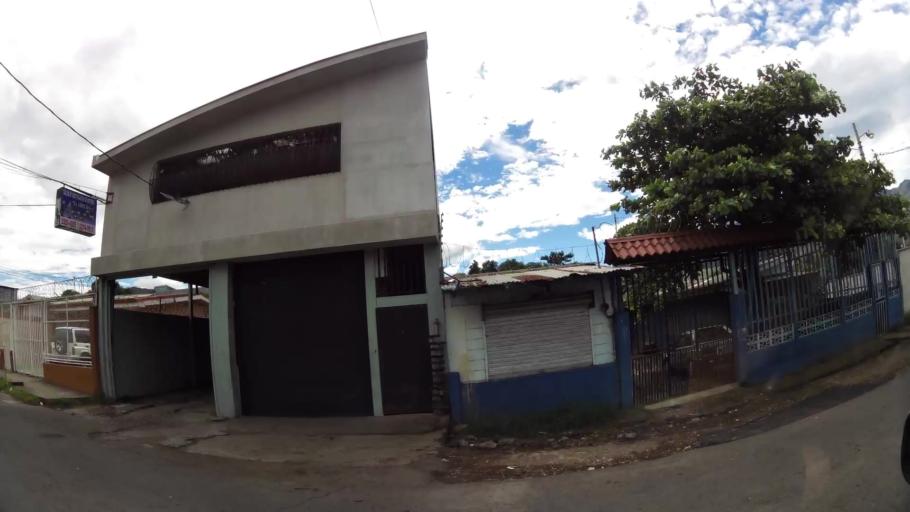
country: CR
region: San Jose
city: San Rafael Arriba
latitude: 9.8944
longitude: -84.0732
